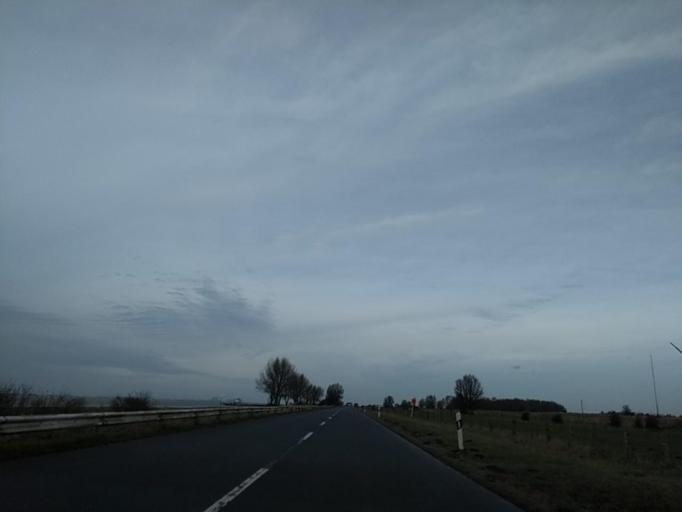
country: NL
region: Groningen
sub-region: Gemeente Delfzijl
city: Delfzijl
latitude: 53.3460
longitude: 7.0131
